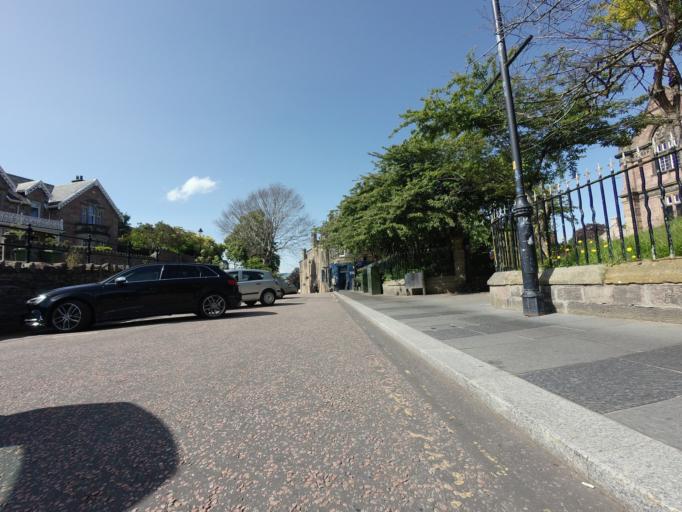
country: GB
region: Scotland
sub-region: Highland
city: Inverness
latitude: 57.4776
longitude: -4.2189
